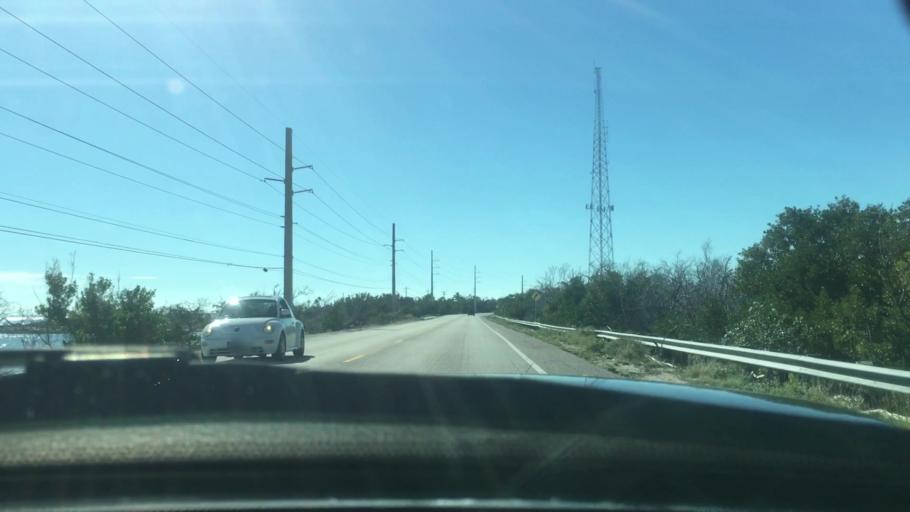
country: US
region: Florida
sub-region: Monroe County
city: Big Pine Key
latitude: 24.6518
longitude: -81.3062
